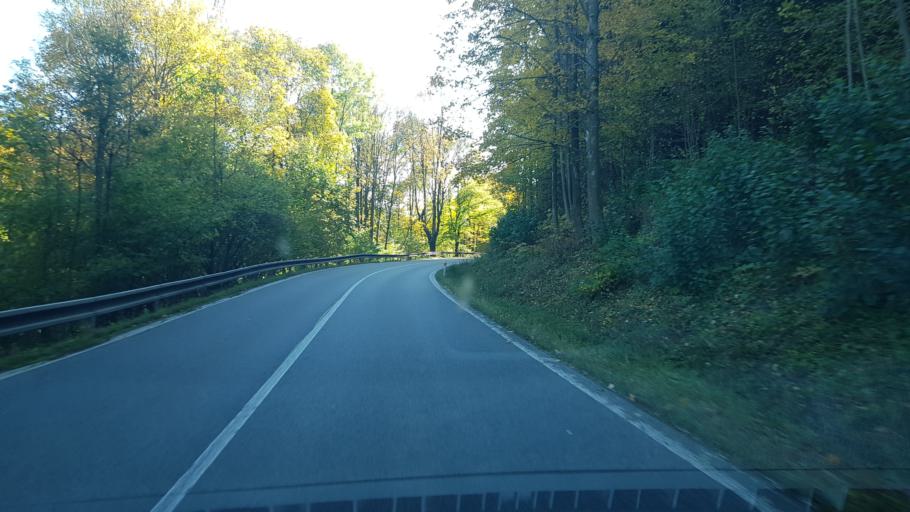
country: CZ
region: Jihocesky
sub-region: Okres Prachatice
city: Vimperk
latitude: 49.0712
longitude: 13.7808
